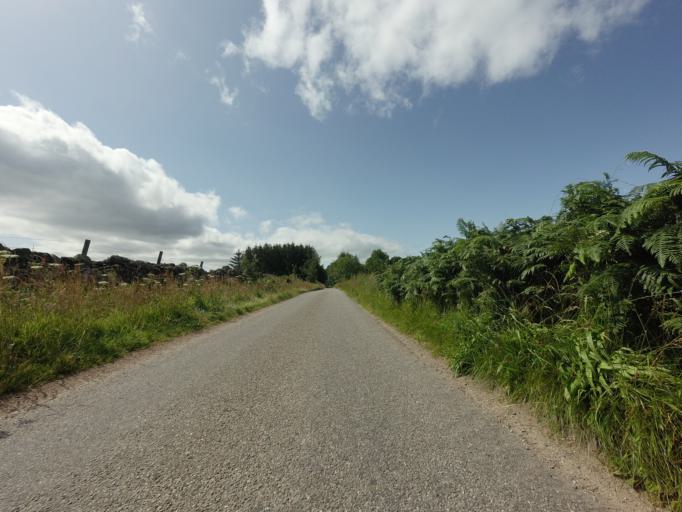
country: GB
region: Scotland
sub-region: Highland
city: Nairn
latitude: 57.4959
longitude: -4.0017
